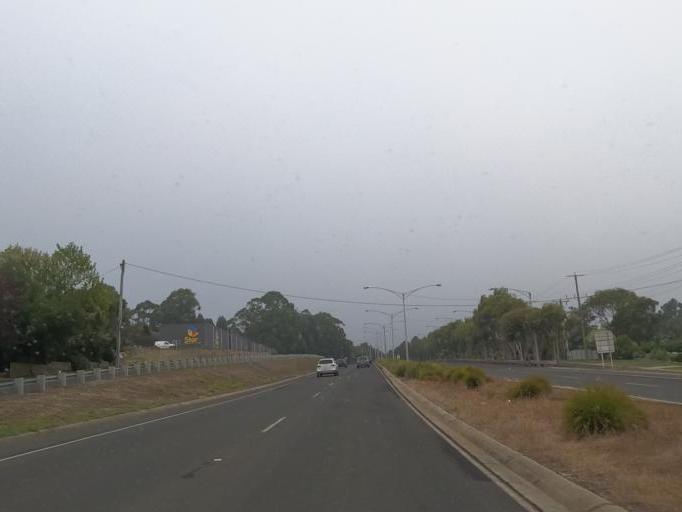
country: AU
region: Victoria
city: Brown Hill
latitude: -37.5592
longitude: 143.9050
